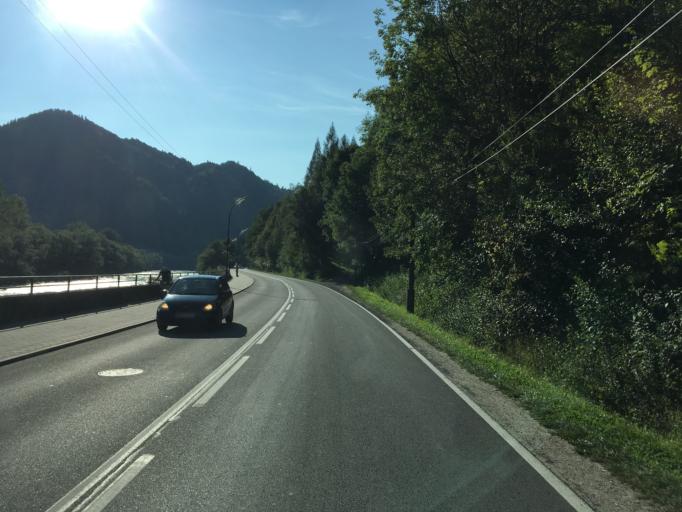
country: PL
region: Lesser Poland Voivodeship
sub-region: Powiat nowotarski
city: Szczawnica
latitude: 49.4261
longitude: 20.4570
